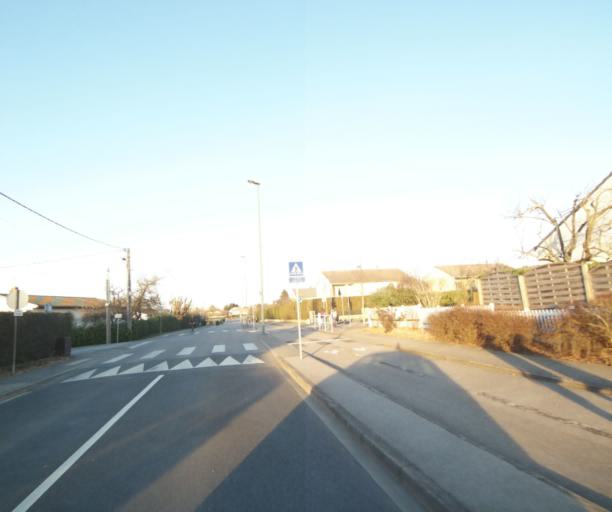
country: FR
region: Lorraine
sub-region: Departement de Meurthe-et-Moselle
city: Seichamps
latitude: 48.7122
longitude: 6.2671
